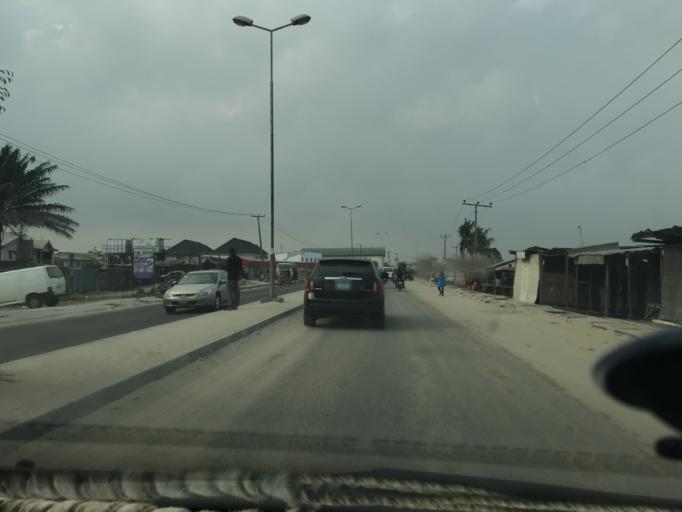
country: NG
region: Lagos
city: Ikoyi
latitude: 6.4798
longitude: 3.5710
